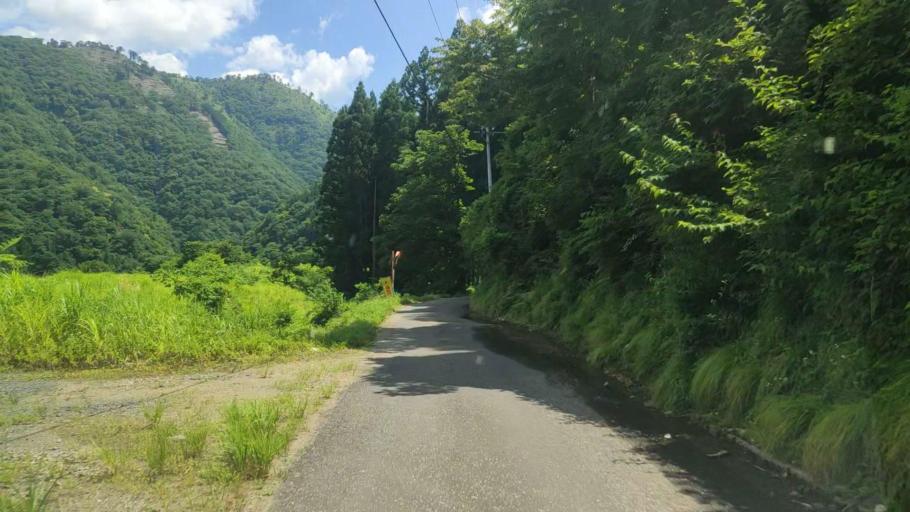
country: JP
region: Fukui
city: Ono
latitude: 35.7486
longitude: 136.5803
